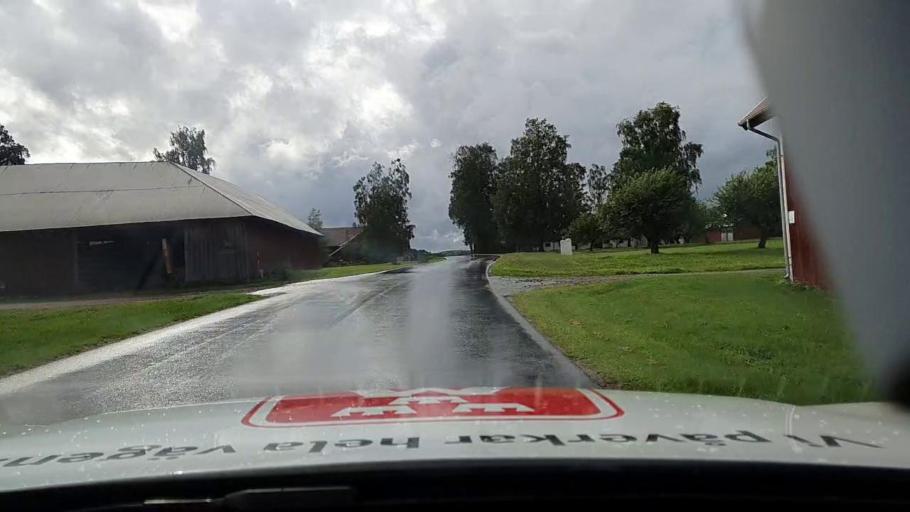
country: SE
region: Vaestra Goetaland
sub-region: Skovde Kommun
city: Stopen
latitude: 58.5288
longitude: 13.9302
